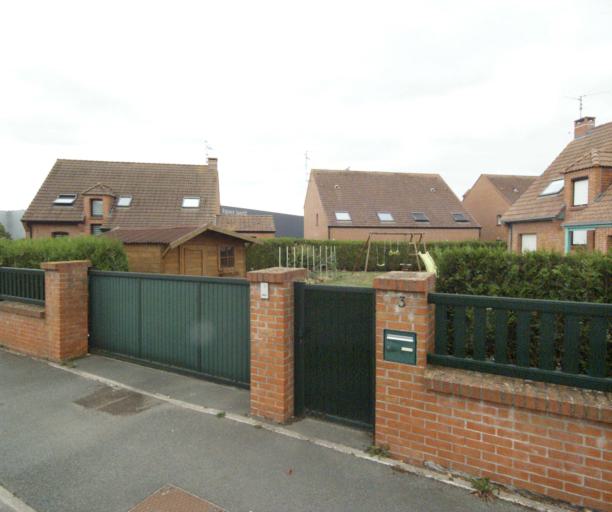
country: FR
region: Nord-Pas-de-Calais
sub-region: Departement du Nord
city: Lesquin
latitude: 50.5872
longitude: 3.1142
